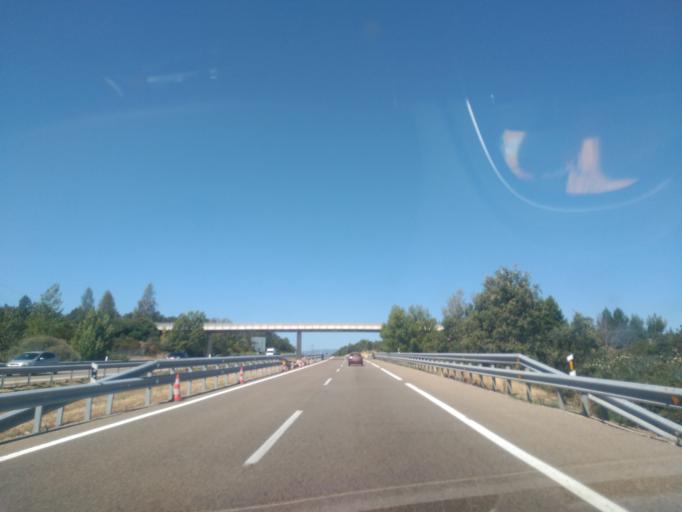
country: ES
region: Castille and Leon
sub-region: Provincia de Zamora
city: Mombuey
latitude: 42.0218
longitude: -6.3611
